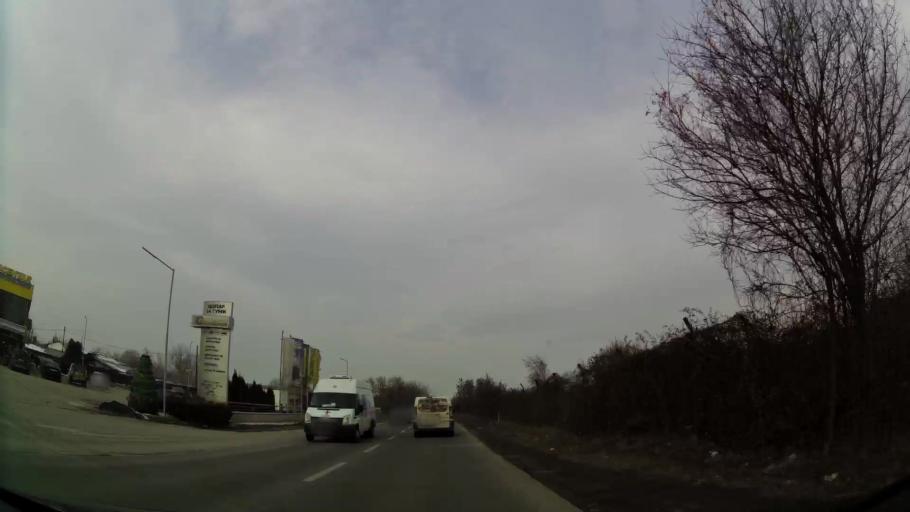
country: MK
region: Suto Orizari
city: Suto Orizare
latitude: 42.0187
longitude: 21.4104
